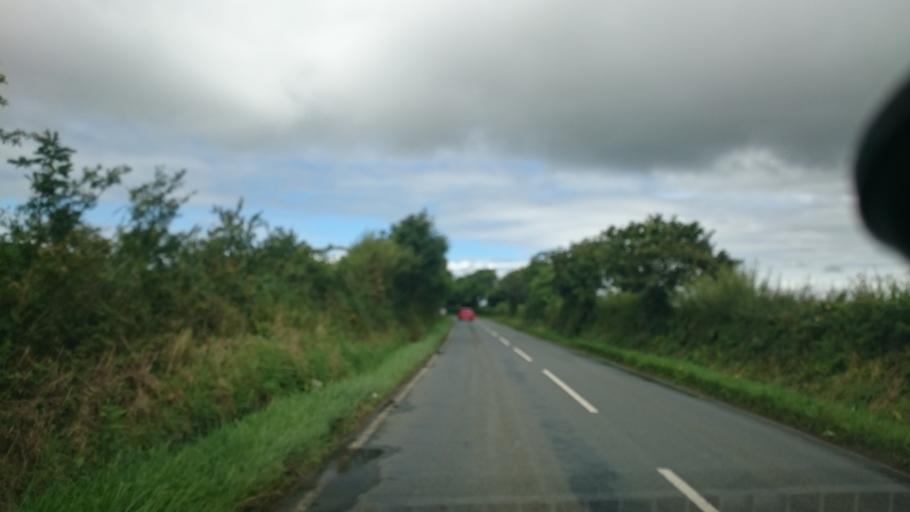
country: GB
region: Wales
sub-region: Pembrokeshire
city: Freystrop
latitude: 51.7485
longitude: -4.9518
